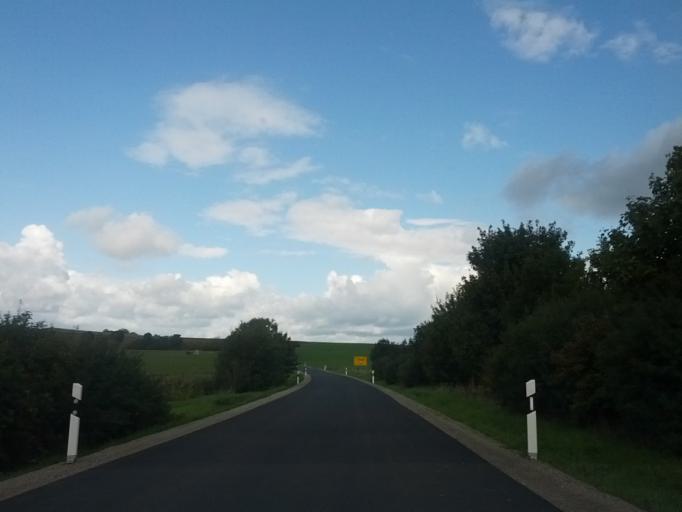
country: DE
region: Hesse
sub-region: Regierungsbezirk Kassel
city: Weissenborn
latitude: 51.0830
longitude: 10.0628
